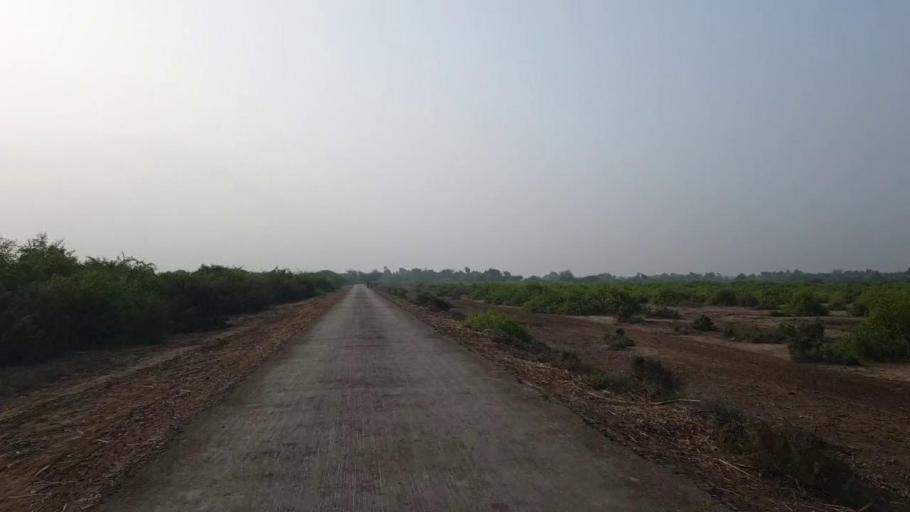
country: PK
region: Sindh
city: Tando Muhammad Khan
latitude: 25.1504
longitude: 68.6058
